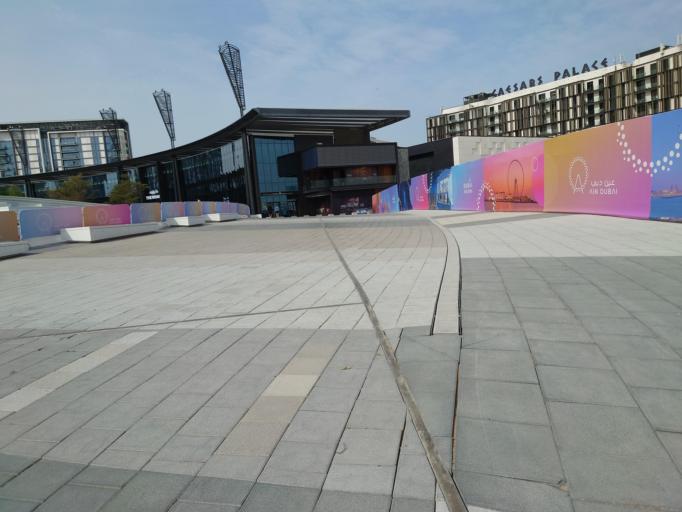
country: AE
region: Dubai
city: Dubai
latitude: 25.0810
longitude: 55.1240
